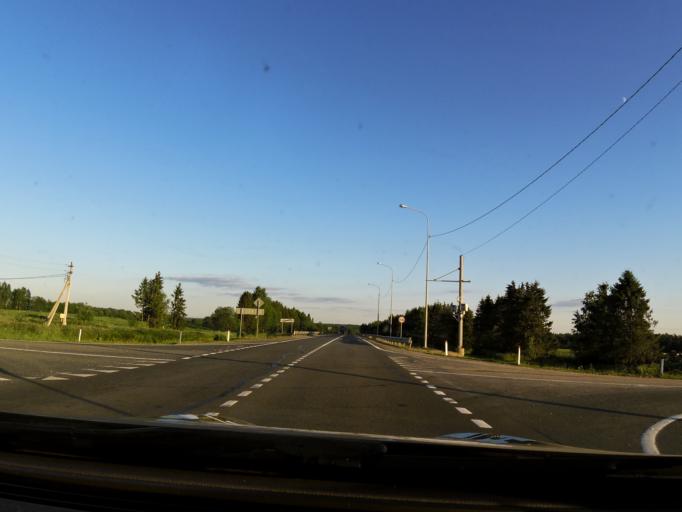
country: RU
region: Vologda
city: Gryazovets
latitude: 58.7062
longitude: 40.2973
